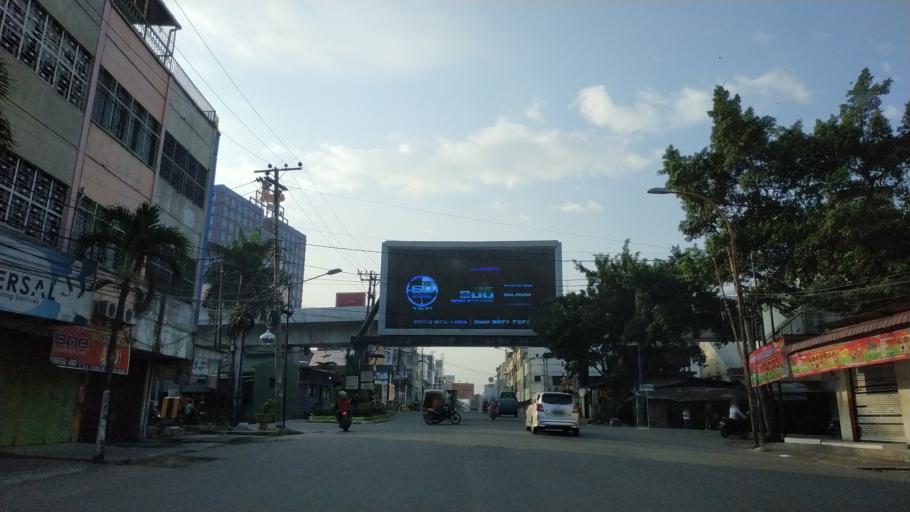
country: ID
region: North Sumatra
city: Medan
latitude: 3.5873
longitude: 98.6910
